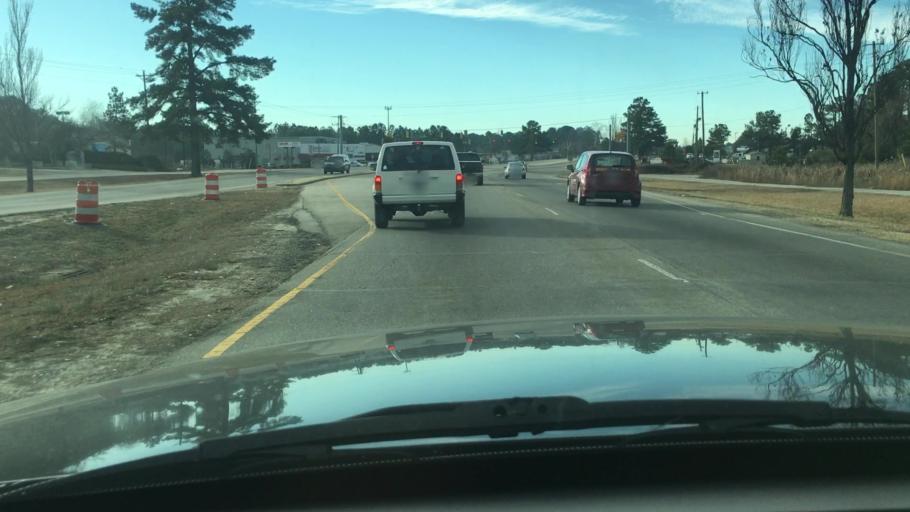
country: US
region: North Carolina
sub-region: Cumberland County
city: Fayetteville
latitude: 35.0019
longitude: -78.8994
